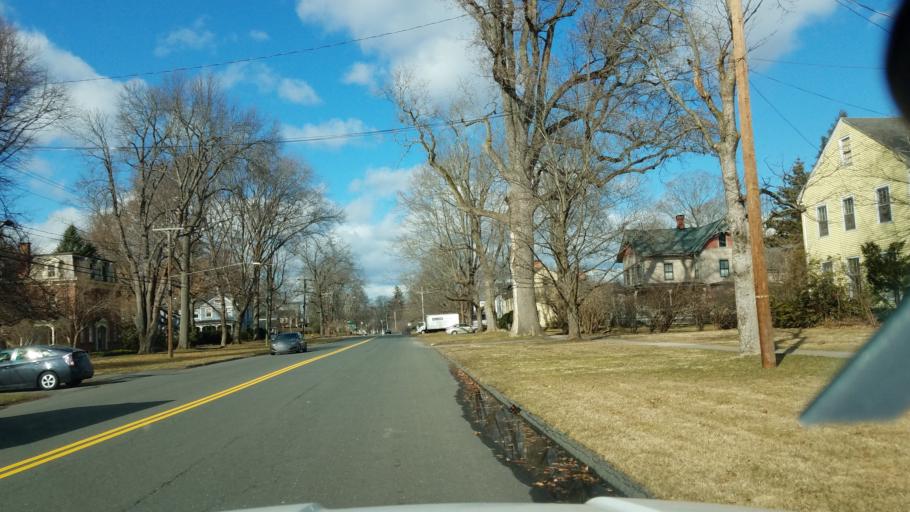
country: US
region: Connecticut
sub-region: Hartford County
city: Wethersfield
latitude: 41.7164
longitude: -72.6526
